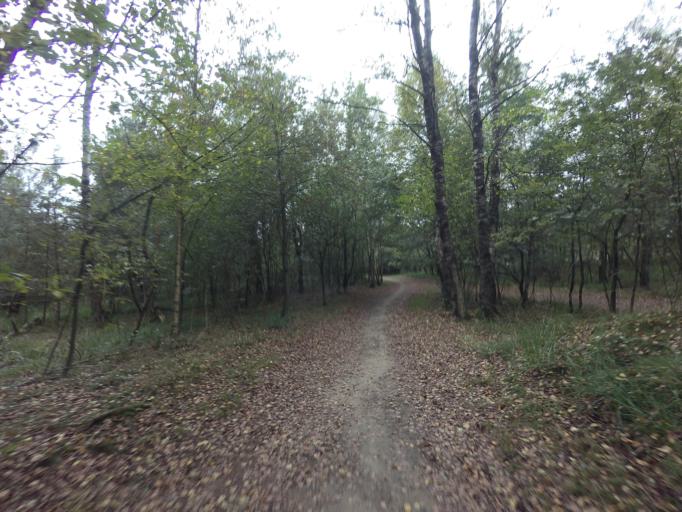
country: DE
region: North Rhine-Westphalia
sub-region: Regierungsbezirk Munster
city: Gronau
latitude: 52.2475
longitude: 7.0930
